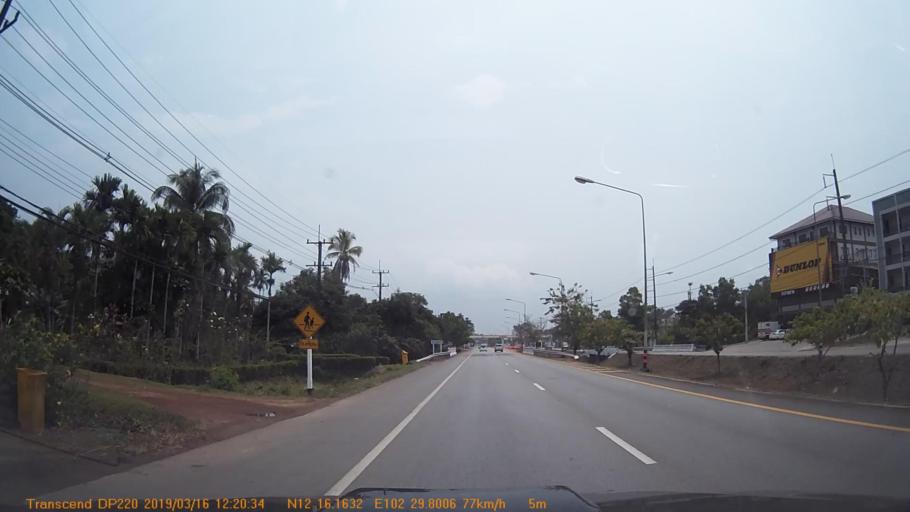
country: TH
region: Trat
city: Trat
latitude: 12.2691
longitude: 102.4969
